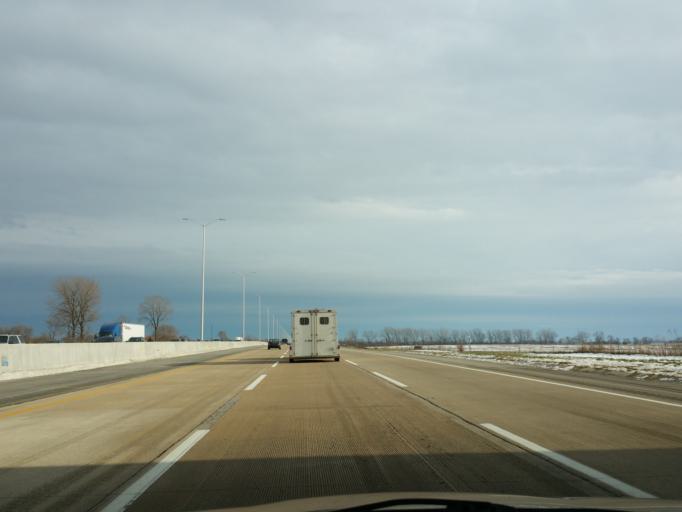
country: US
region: Illinois
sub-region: Boone County
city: Belvidere
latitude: 42.2196
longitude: -88.7499
